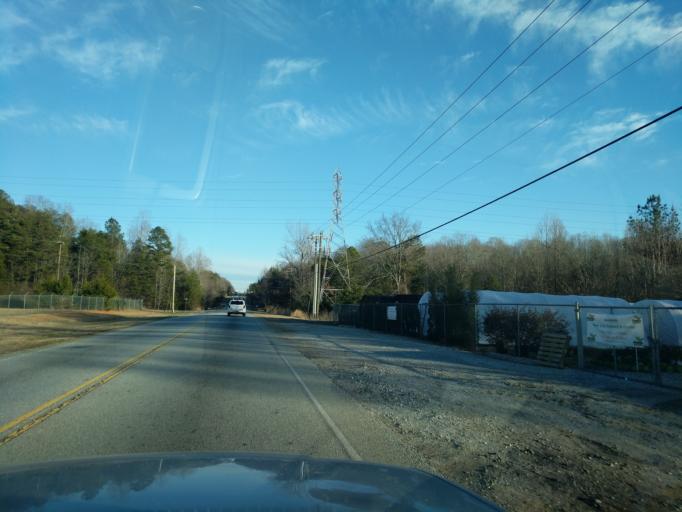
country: US
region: South Carolina
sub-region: Anderson County
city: Williamston
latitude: 34.6416
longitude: -82.4471
